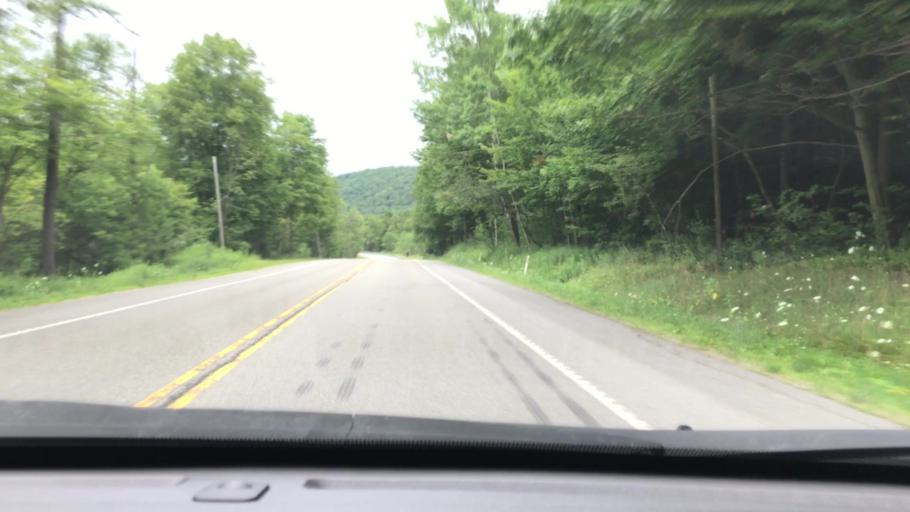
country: US
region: Pennsylvania
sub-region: McKean County
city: Bradford
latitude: 41.8472
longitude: -78.6838
